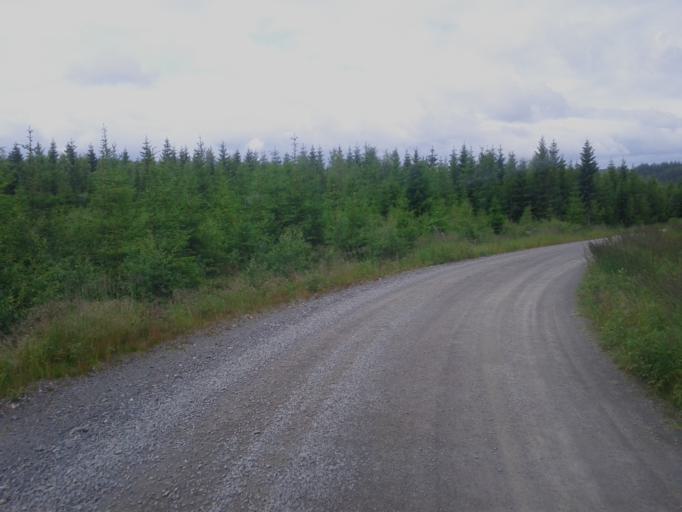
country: SE
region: Vaesternorrland
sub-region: OErnskoeldsviks Kommun
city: Bjasta
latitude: 63.1209
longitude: 18.4113
